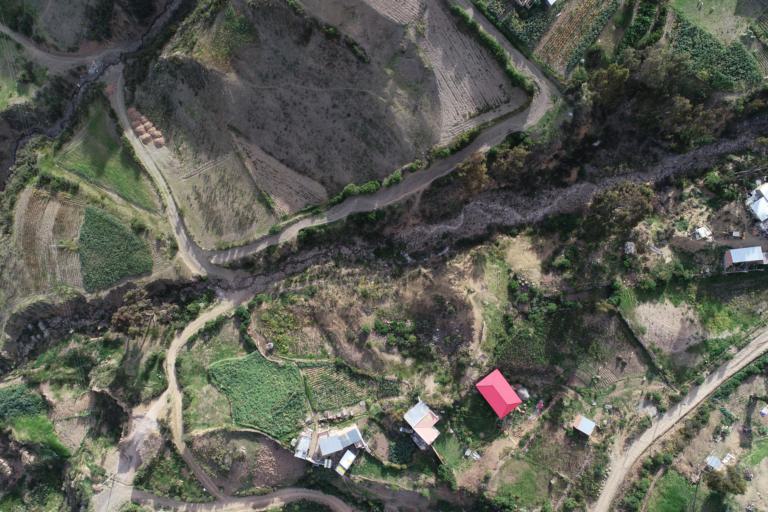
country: BO
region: La Paz
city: La Paz
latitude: -16.5463
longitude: -67.9957
